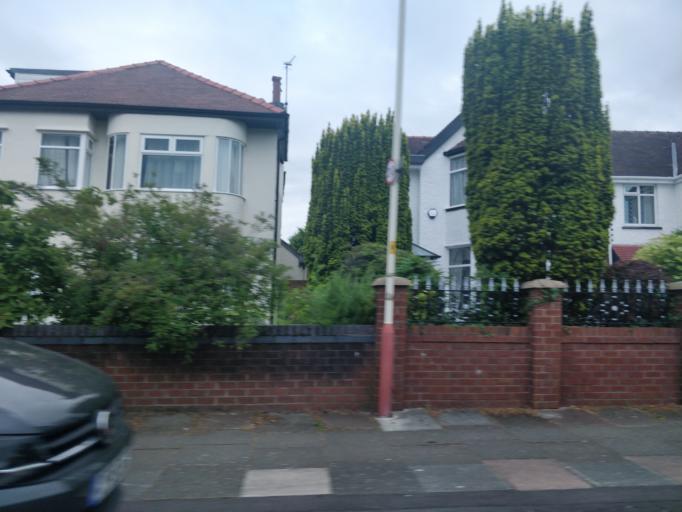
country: GB
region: England
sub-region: Sefton
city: Southport
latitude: 53.6624
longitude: -2.9707
